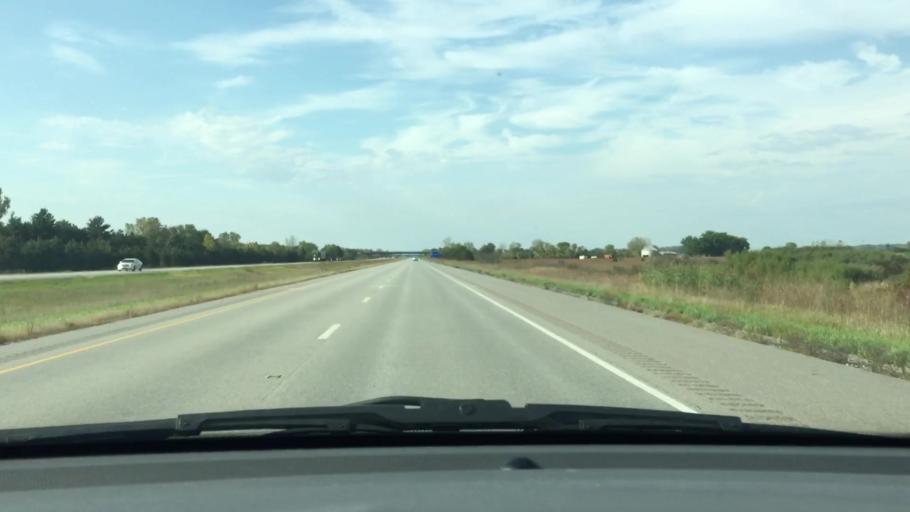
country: US
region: Illinois
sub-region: Rock Island County
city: Port Byron
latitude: 41.5773
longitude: -90.2152
